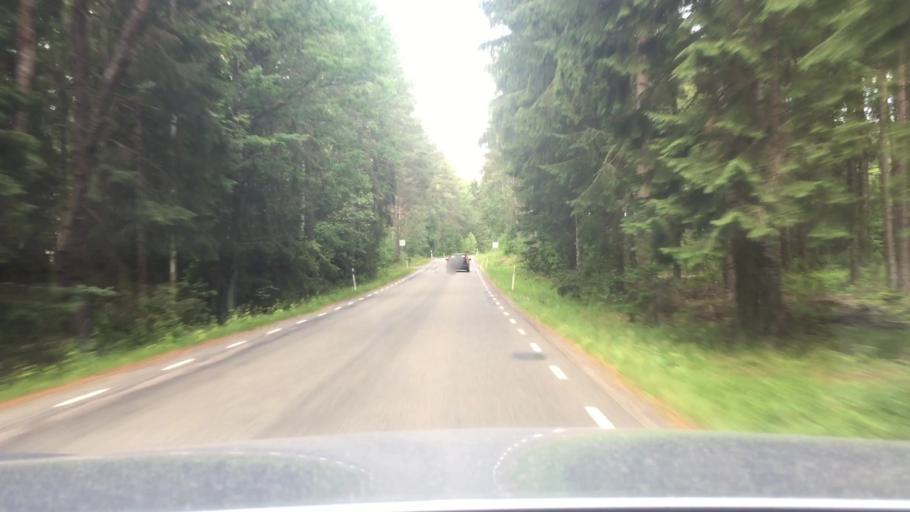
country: SE
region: Vaestra Goetaland
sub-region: Tidaholms Kommun
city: Tidaholm
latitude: 58.2025
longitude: 13.9801
